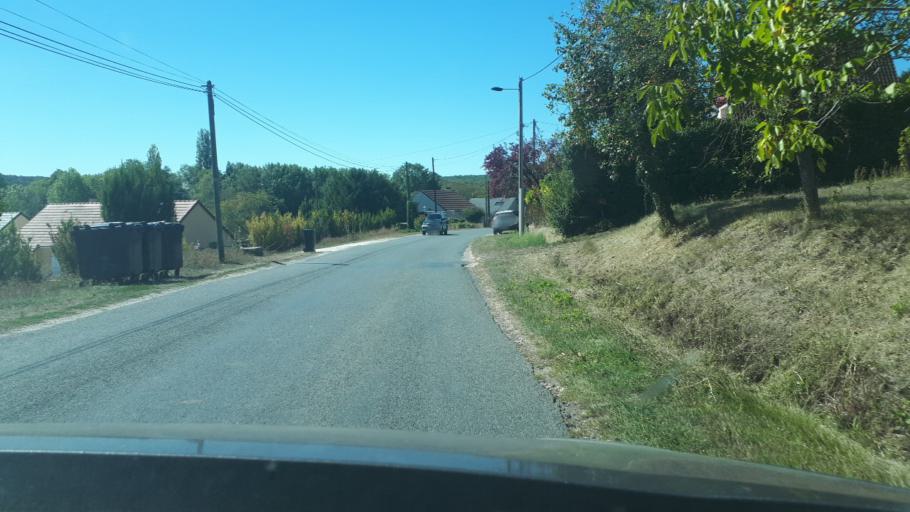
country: FR
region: Centre
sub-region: Departement du Cher
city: Sancerre
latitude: 47.2607
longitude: 2.7622
